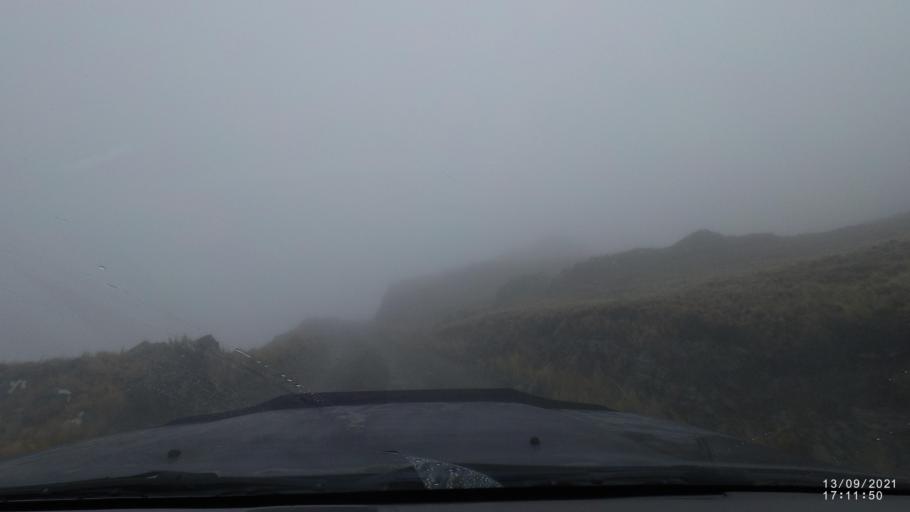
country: BO
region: Cochabamba
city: Colomi
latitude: -17.3375
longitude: -65.7442
